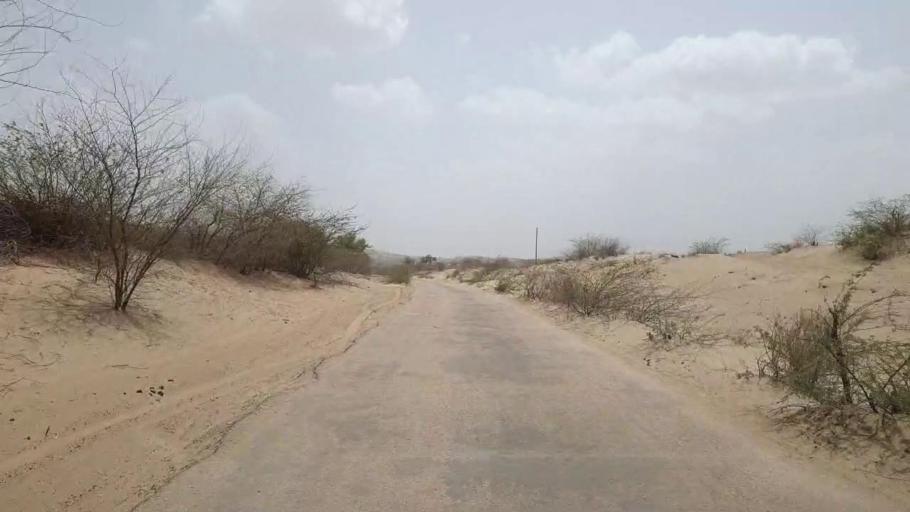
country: PK
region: Sindh
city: Diplo
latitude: 24.3692
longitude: 69.4050
